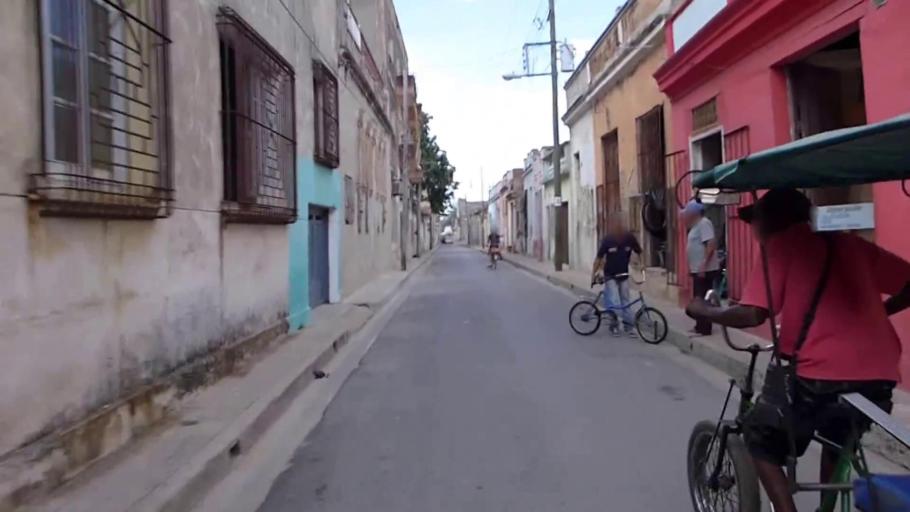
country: CU
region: Camaguey
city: Camaguey
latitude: 21.3867
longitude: -77.9168
